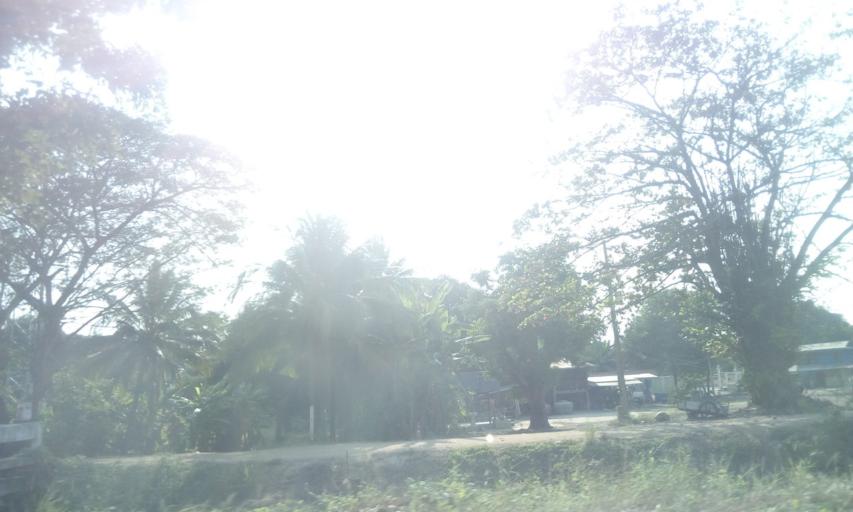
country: TH
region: Sing Buri
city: Phrom Buri
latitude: 14.8395
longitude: 100.4336
